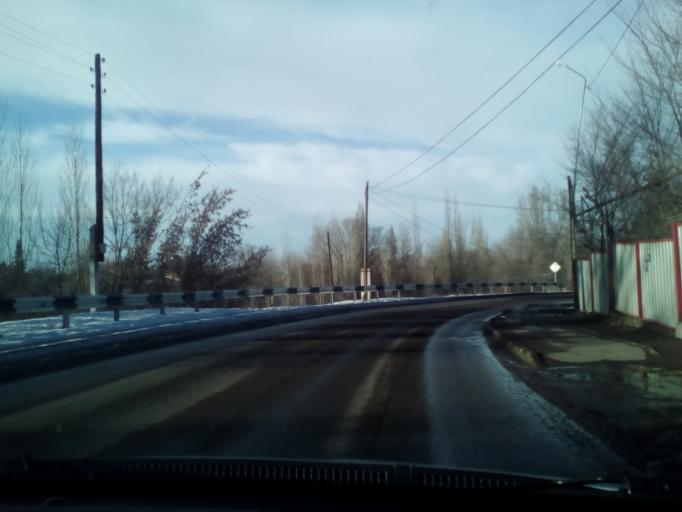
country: KZ
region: Almaty Oblysy
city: Burunday
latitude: 43.1599
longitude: 76.4171
